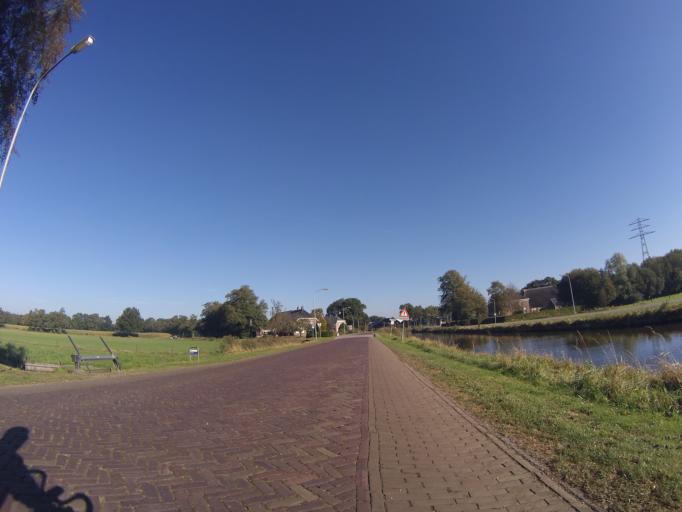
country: NL
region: Drenthe
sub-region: Gemeente Coevorden
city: Dalen
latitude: 52.7290
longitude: 6.6781
